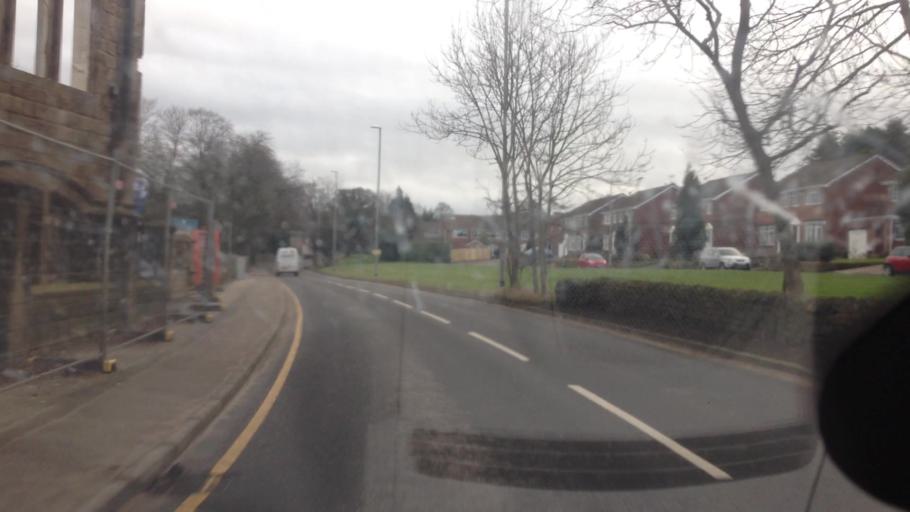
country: GB
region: England
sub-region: City and Borough of Leeds
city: Yeadon
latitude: 53.8587
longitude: -1.6844
